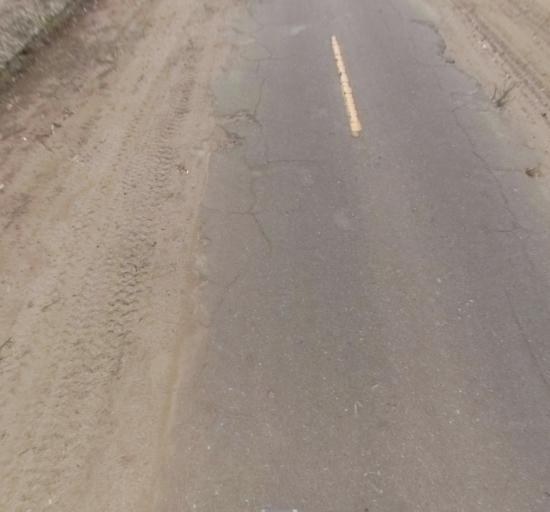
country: US
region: California
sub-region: Madera County
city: Chowchilla
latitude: 37.0761
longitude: -120.3772
